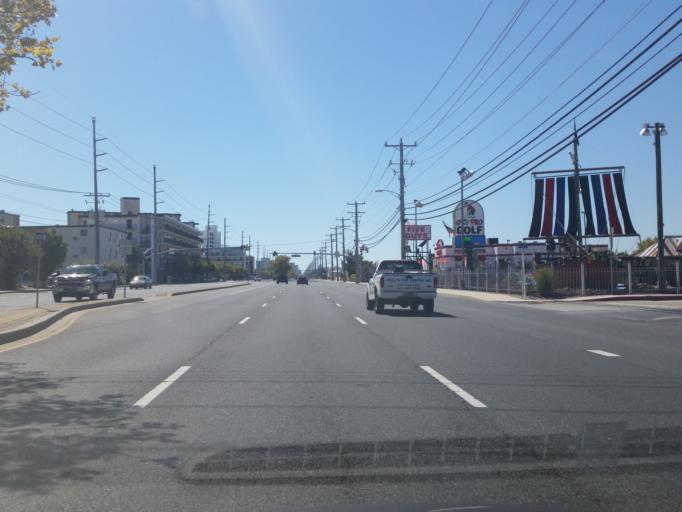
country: US
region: Delaware
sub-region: Sussex County
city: Bethany Beach
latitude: 38.4428
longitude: -75.0533
